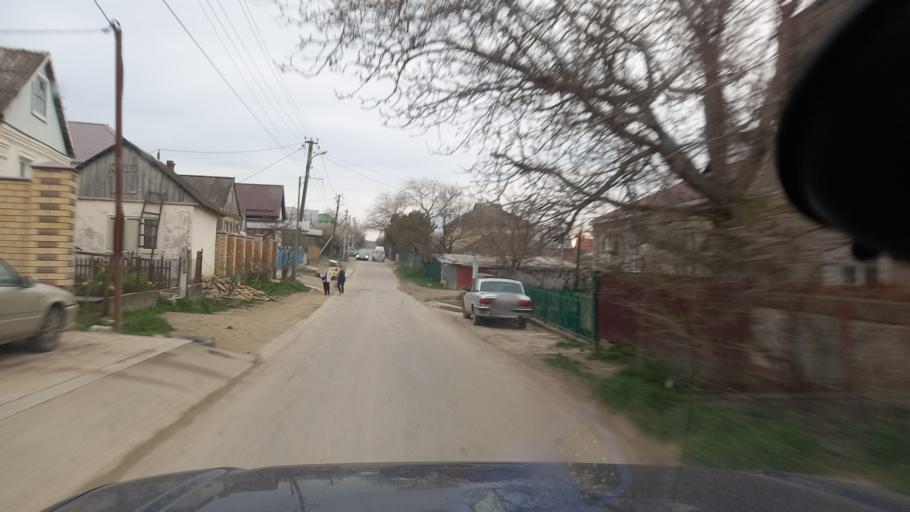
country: RU
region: Krasnodarskiy
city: Anapa
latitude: 44.8503
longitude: 37.3572
